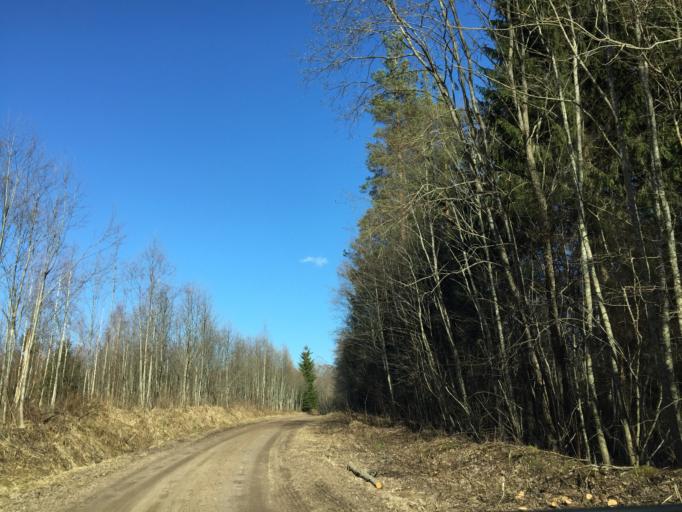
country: LV
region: Ropazu
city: Ropazi
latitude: 56.9025
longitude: 24.7433
